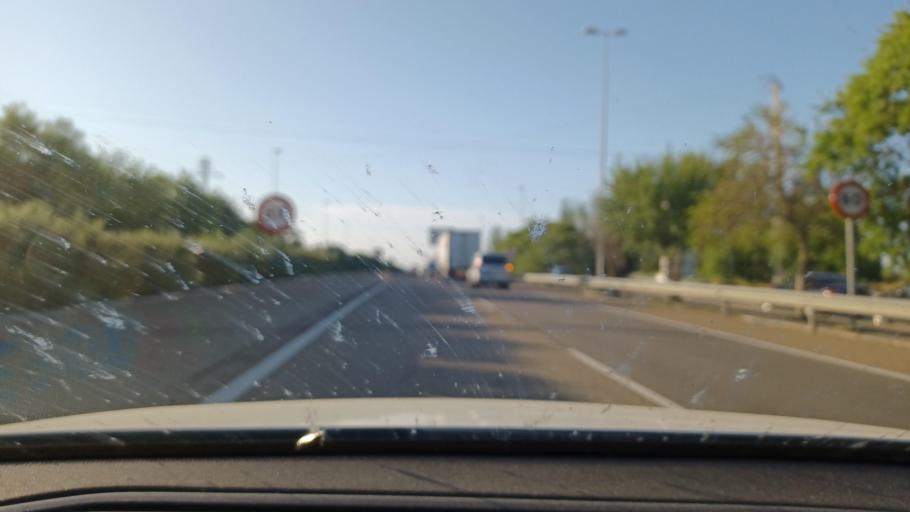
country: ES
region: Castille and Leon
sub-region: Provincia de Valladolid
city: Cisterniga
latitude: 41.6093
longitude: -4.7092
